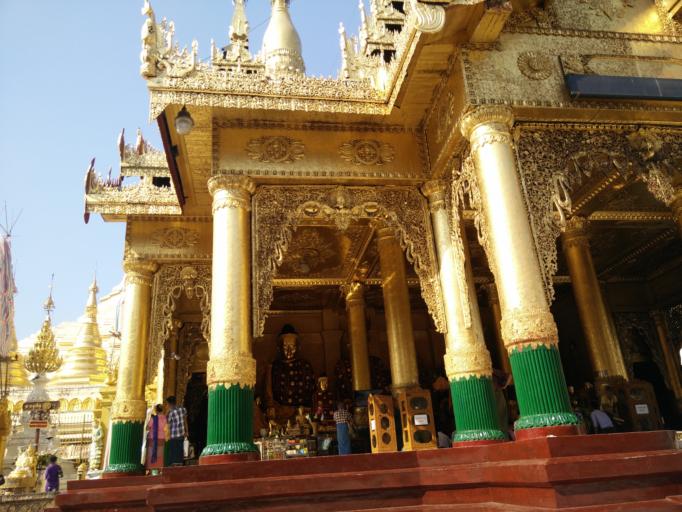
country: MM
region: Yangon
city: Yangon
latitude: 16.7985
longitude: 96.1503
